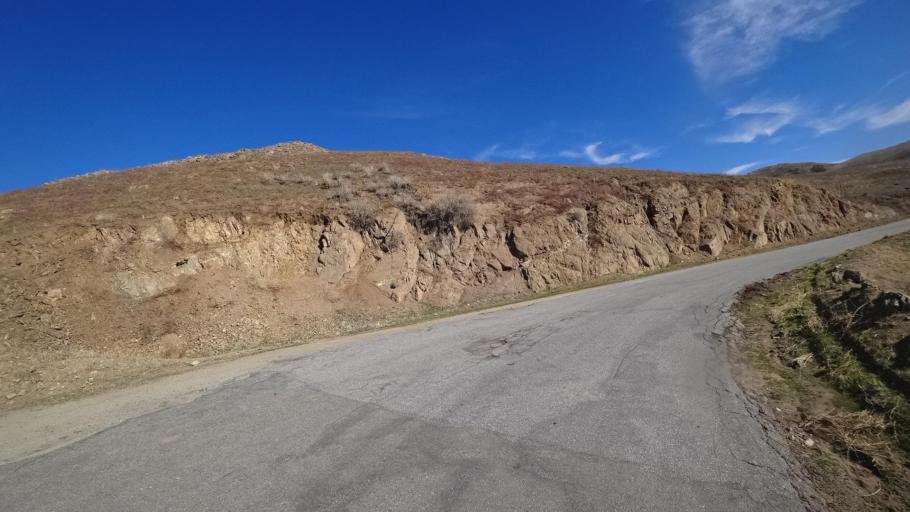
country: US
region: California
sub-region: Kern County
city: Arvin
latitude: 35.4169
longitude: -118.7481
